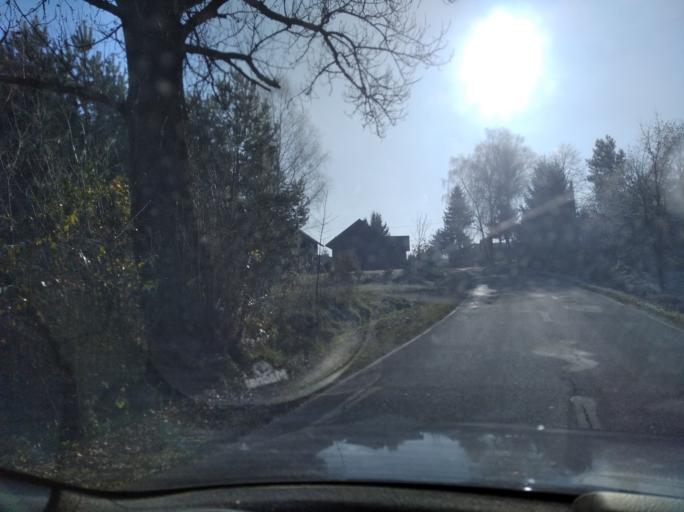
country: PL
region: Subcarpathian Voivodeship
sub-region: Powiat strzyzowski
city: Wysoka Strzyzowska
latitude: 49.8364
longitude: 21.7395
